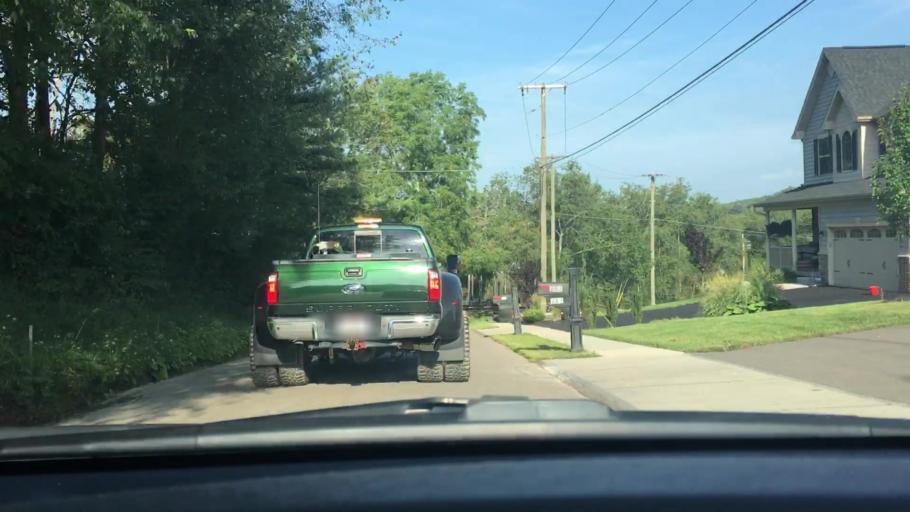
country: US
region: Pennsylvania
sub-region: Butler County
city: Zelienople
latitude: 40.7715
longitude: -80.1104
